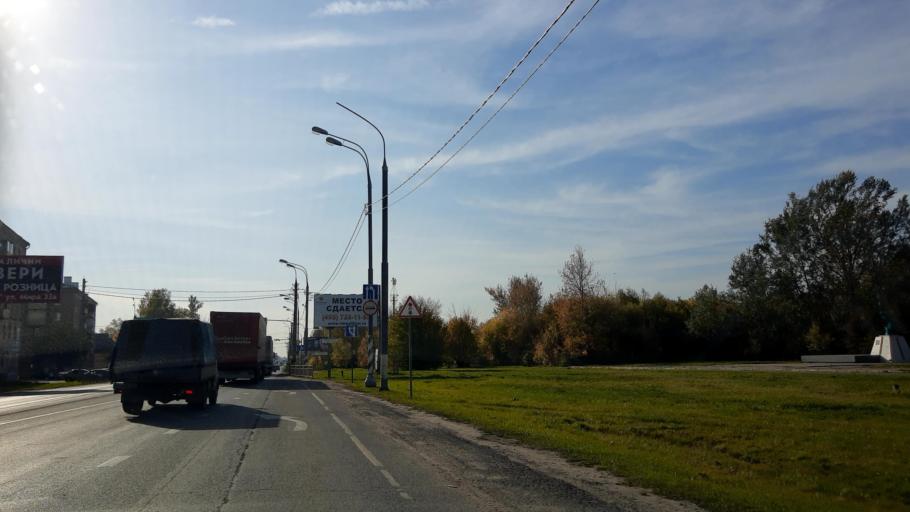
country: RU
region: Moskovskaya
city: Elektrostal'
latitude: 55.7911
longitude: 38.4306
